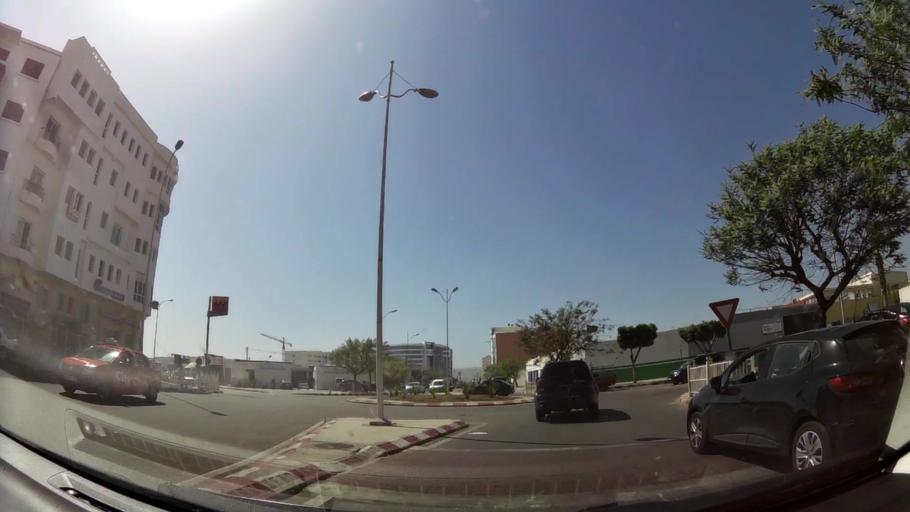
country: MA
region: Oued ed Dahab-Lagouira
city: Dakhla
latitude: 30.4167
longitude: -9.5735
